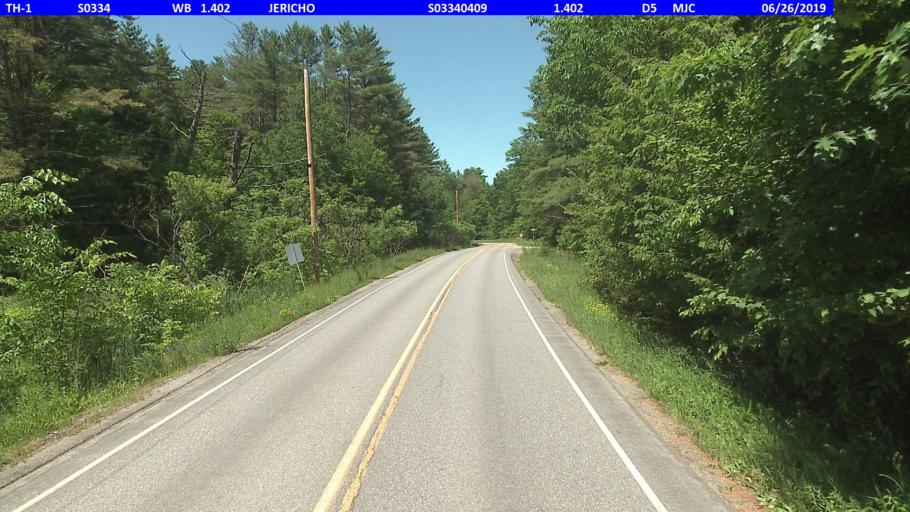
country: US
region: Vermont
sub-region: Chittenden County
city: Jericho
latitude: 44.4599
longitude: -72.9929
